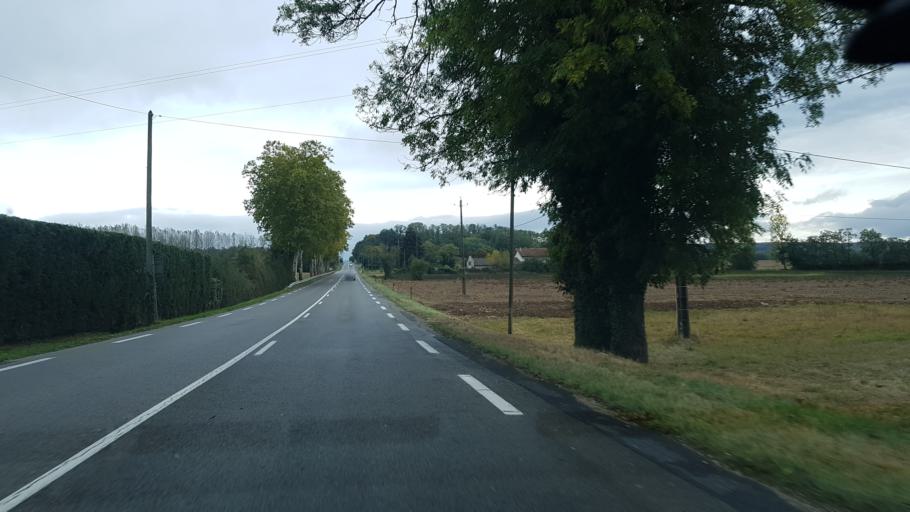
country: FR
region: Rhone-Alpes
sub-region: Departement de l'Ain
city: Saint-Martin-du-Mont
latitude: 46.0893
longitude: 5.3153
